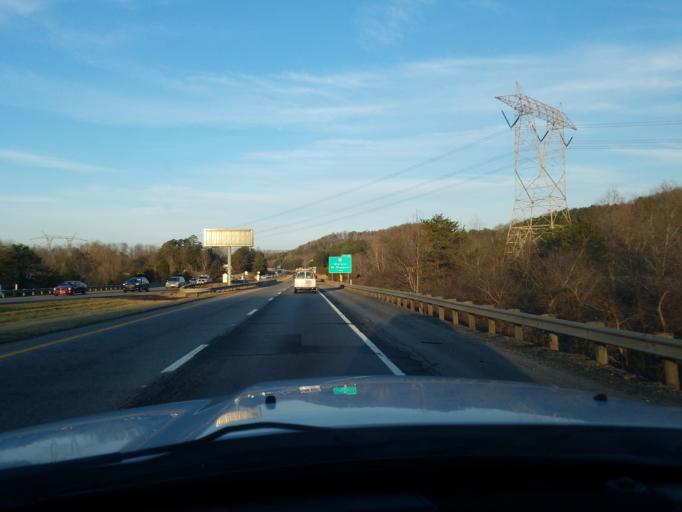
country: US
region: West Virginia
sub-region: Kanawha County
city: Nitro
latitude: 38.4553
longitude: -81.8759
